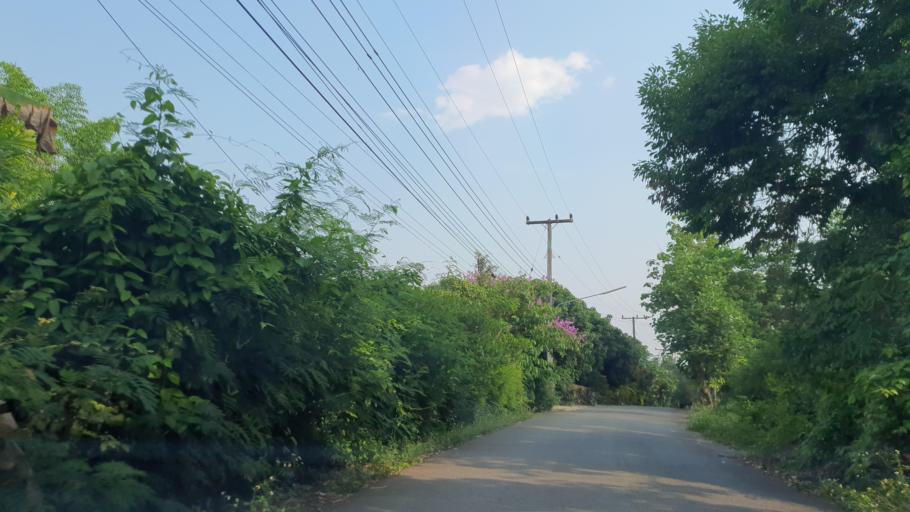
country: TH
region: Chiang Mai
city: Mae Wang
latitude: 18.6755
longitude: 98.8119
